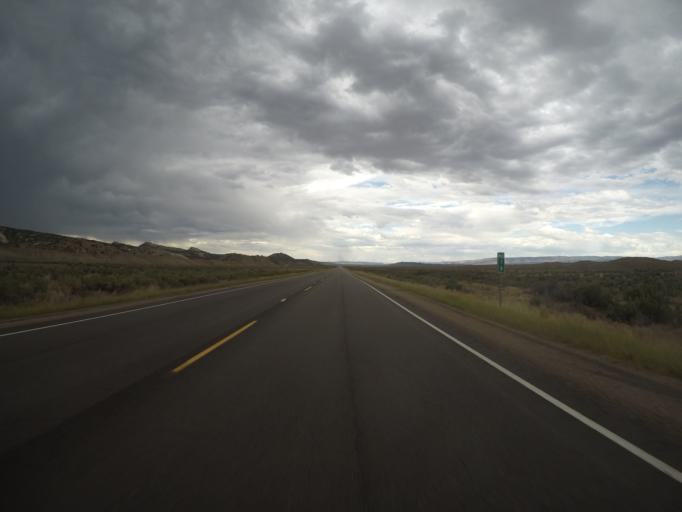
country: US
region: Colorado
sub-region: Rio Blanco County
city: Rangely
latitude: 40.2501
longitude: -108.7686
